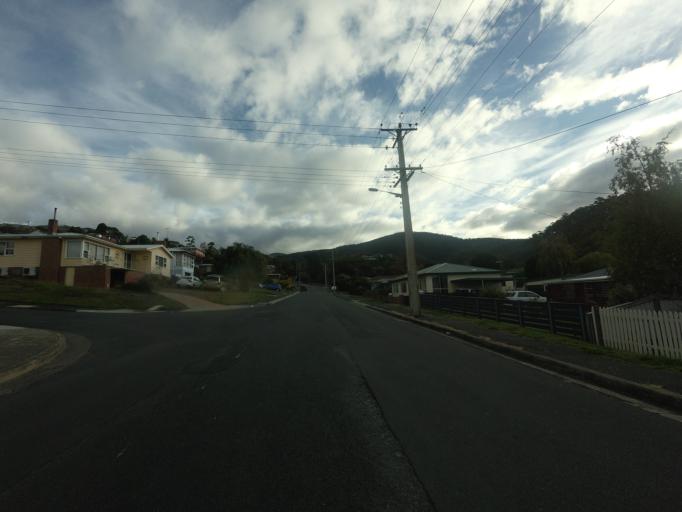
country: AU
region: Tasmania
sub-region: Glenorchy
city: Berriedale
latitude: -42.8282
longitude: 147.2599
